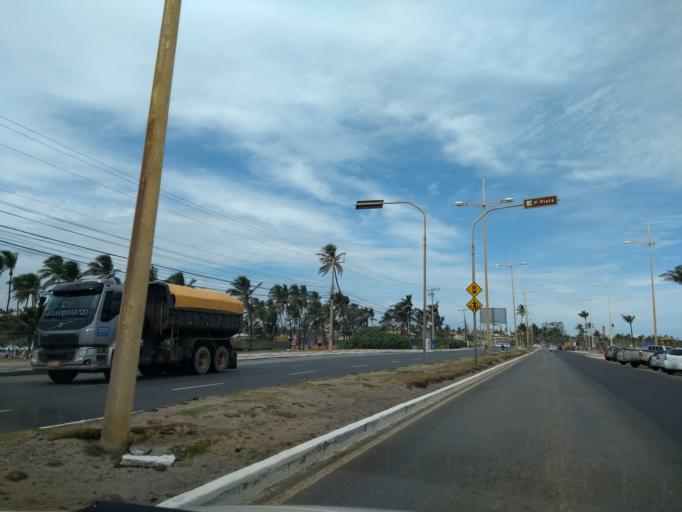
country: BR
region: Bahia
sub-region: Lauro De Freitas
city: Lauro de Freitas
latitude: -12.9563
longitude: -38.3880
